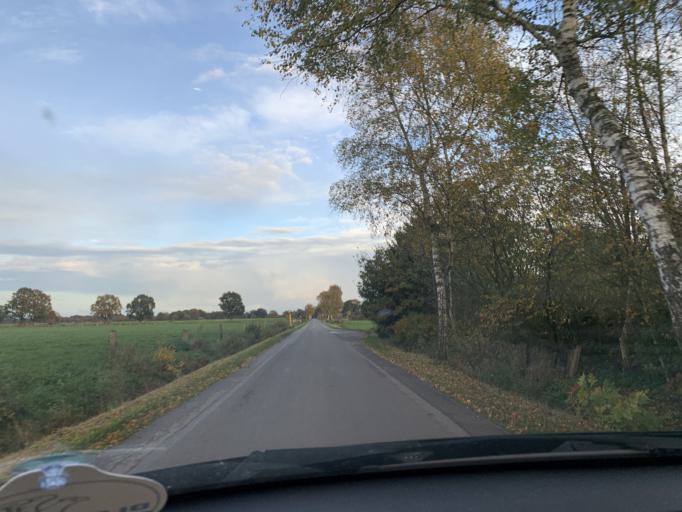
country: DE
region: Lower Saxony
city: Wiefelstede
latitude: 53.2513
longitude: 8.0700
